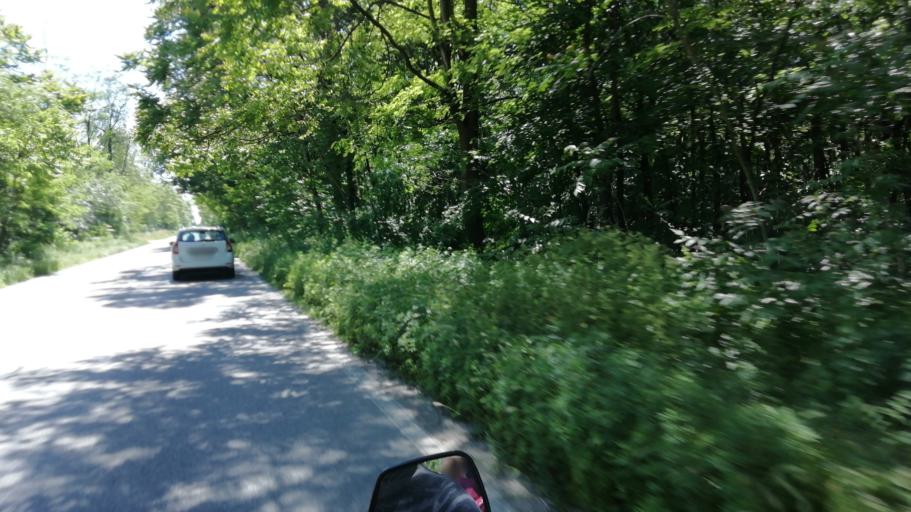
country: IT
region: Lombardy
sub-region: Provincia di Varese
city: Lonate Pozzolo
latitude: 45.5878
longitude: 8.7310
